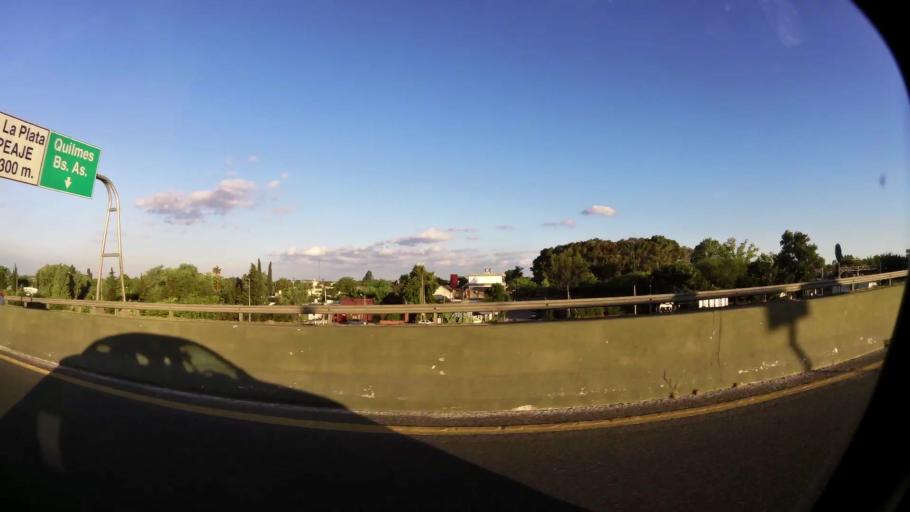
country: AR
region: Buenos Aires
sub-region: Partido de Quilmes
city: Quilmes
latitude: -34.7896
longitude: -58.1565
